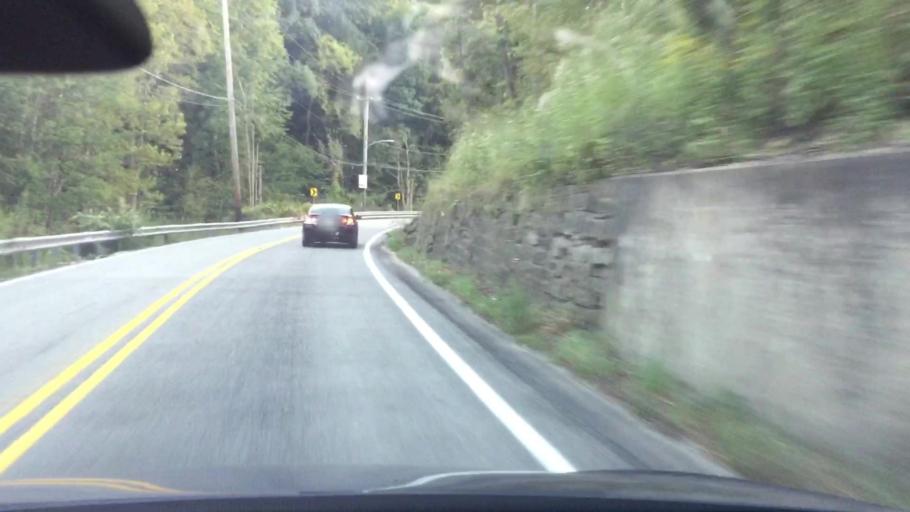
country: US
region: Pennsylvania
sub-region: Allegheny County
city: Sharpsburg
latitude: 40.5294
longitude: -79.9238
